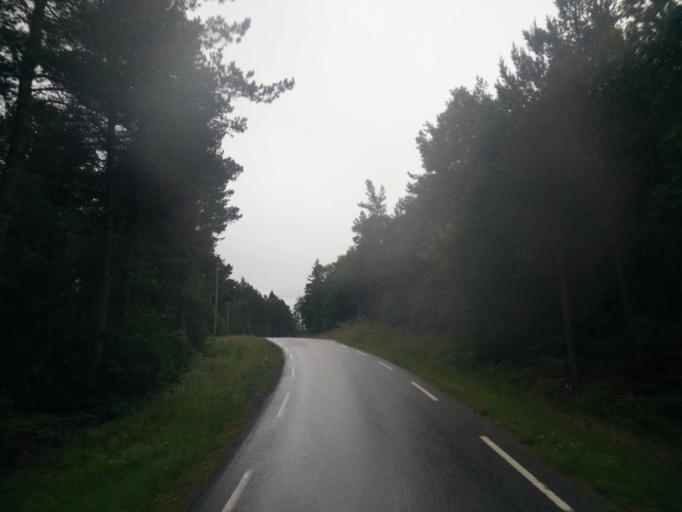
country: NO
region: More og Romsdal
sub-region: Kristiansund
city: Rensvik
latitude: 63.0248
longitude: 7.8990
